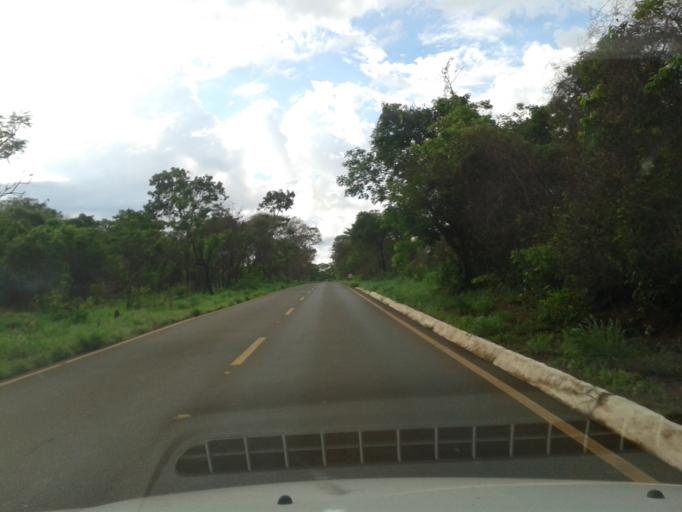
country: BR
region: Minas Gerais
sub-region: Santa Vitoria
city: Santa Vitoria
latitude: -18.9560
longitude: -49.8129
